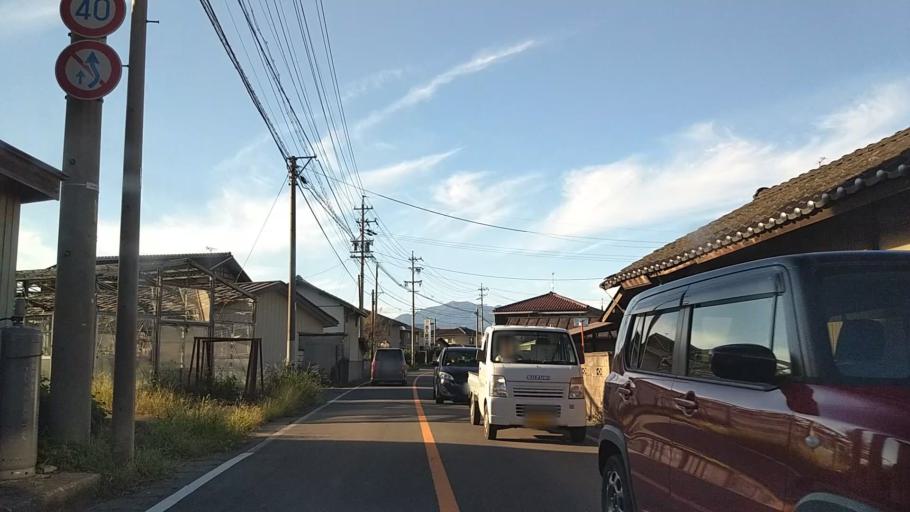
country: JP
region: Nagano
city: Nagano-shi
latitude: 36.5869
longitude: 138.1985
